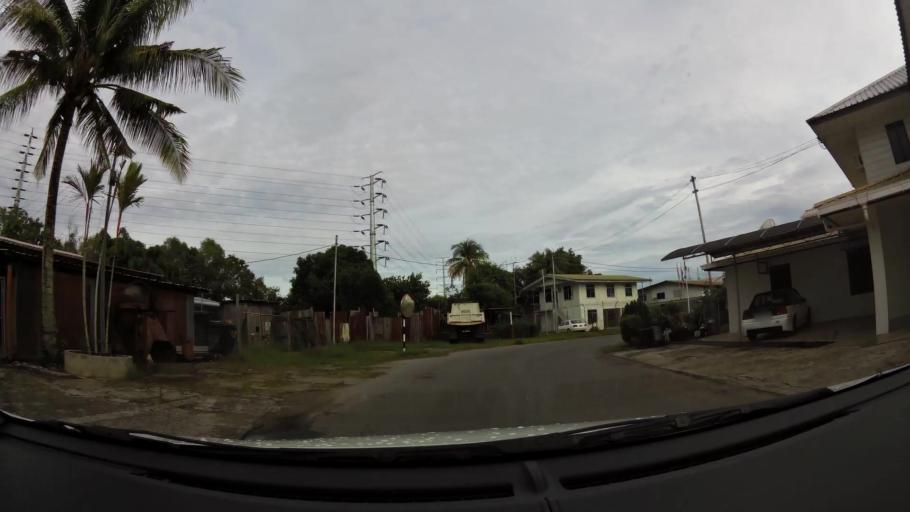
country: BN
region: Belait
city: Seria
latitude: 4.6145
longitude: 114.3479
